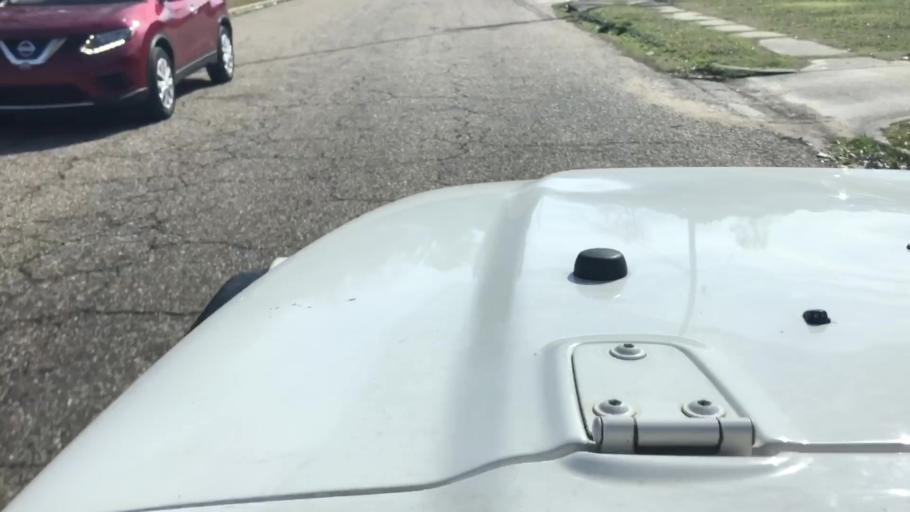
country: US
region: Alabama
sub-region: Elmore County
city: Blue Ridge
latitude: 32.4052
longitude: -86.1868
